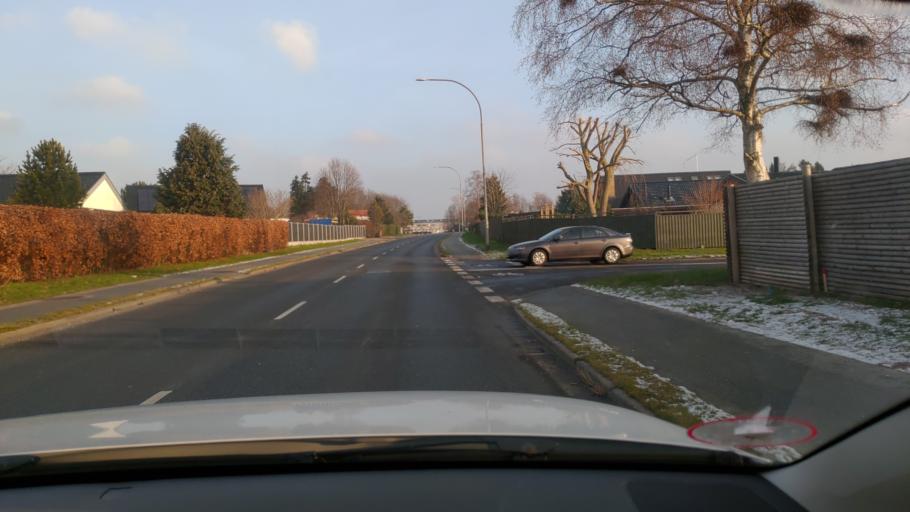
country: DK
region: Zealand
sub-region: Solrod Kommune
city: Solrod Strand
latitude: 55.5418
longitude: 12.2219
